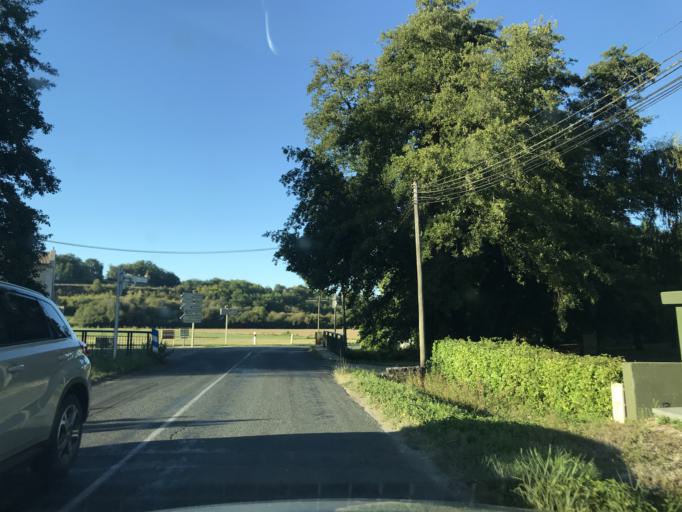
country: FR
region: Aquitaine
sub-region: Departement de la Gironde
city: Rauzan
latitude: 44.7529
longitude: -0.0740
